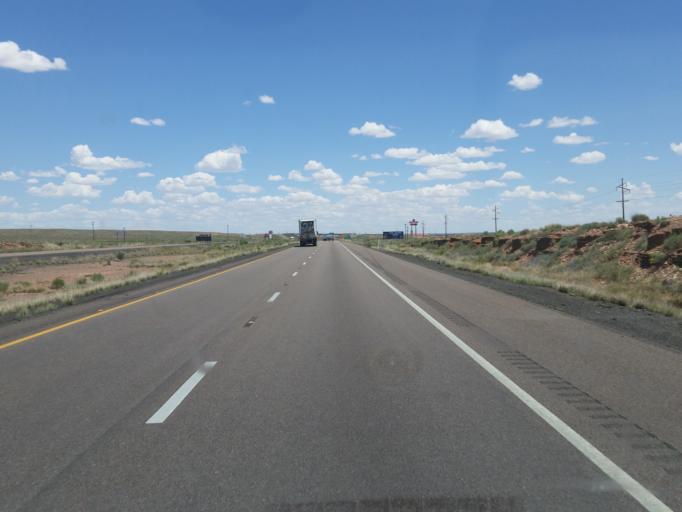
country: US
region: Arizona
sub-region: Navajo County
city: Holbrook
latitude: 34.9088
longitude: -110.2260
